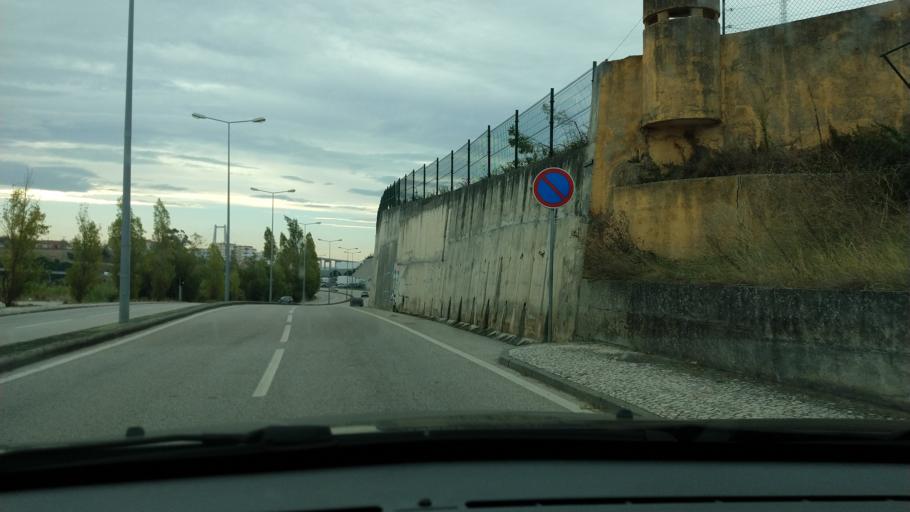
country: PT
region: Coimbra
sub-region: Figueira da Foz
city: Figueira da Foz
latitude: 40.1552
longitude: -8.8500
